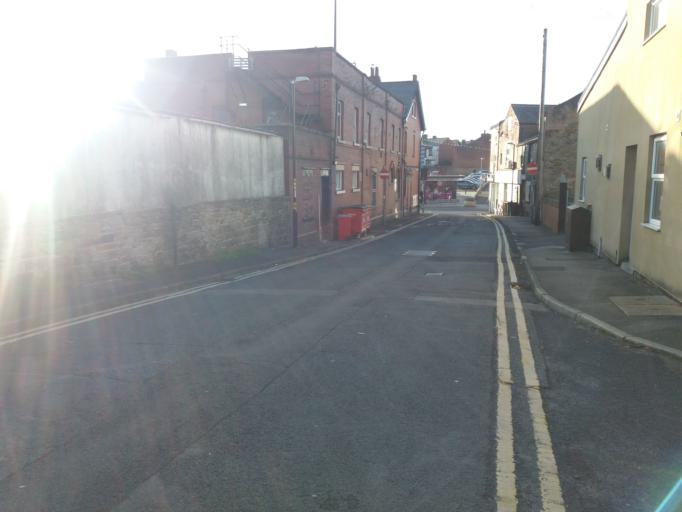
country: GB
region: England
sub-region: Lancashire
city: Chorley
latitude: 53.6513
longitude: -2.6308
